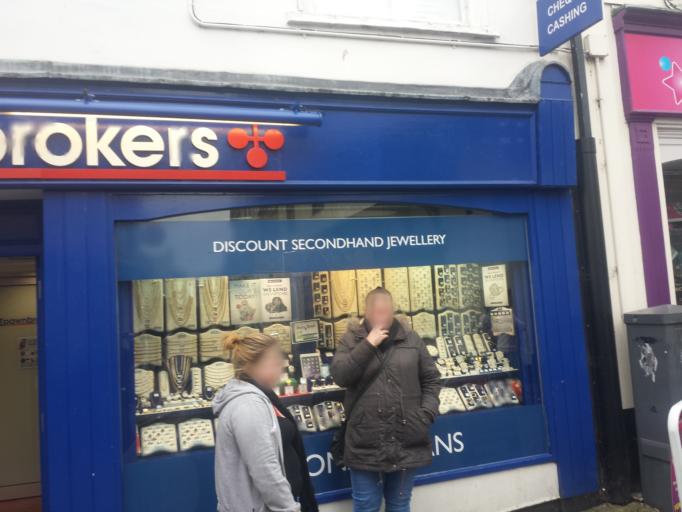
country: GB
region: England
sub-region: Essex
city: Colchester
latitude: 51.8881
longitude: 0.9024
